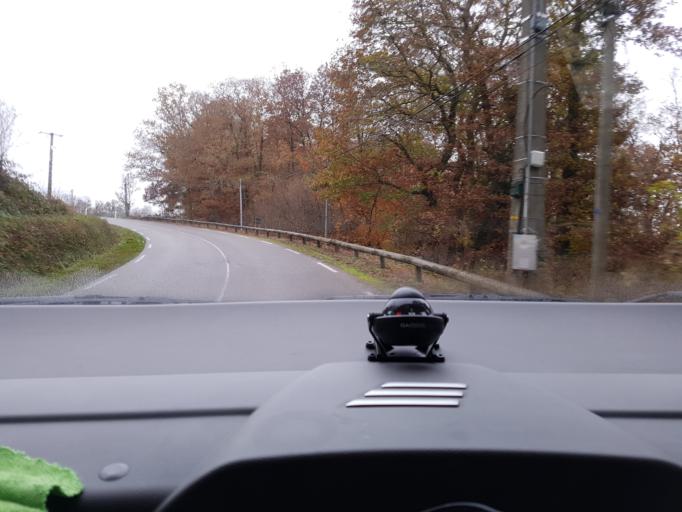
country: FR
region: Haute-Normandie
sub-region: Departement de l'Eure
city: Beaumont-le-Roger
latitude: 48.9825
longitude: 0.7857
